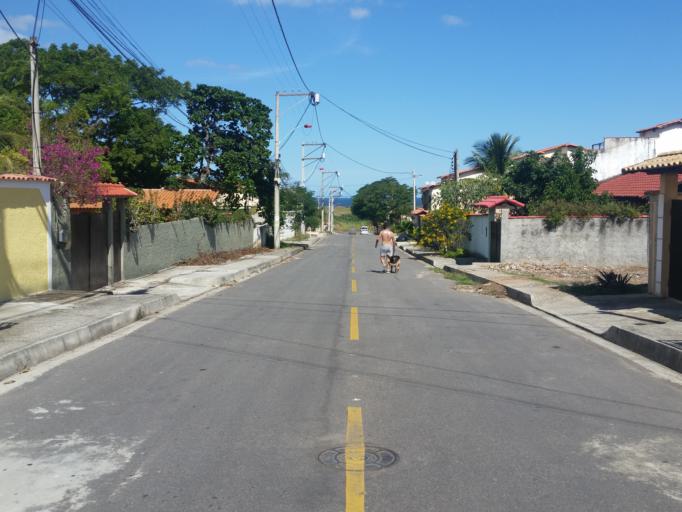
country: BR
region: Rio de Janeiro
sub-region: Marica
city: Marica
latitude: -22.9661
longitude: -42.9667
